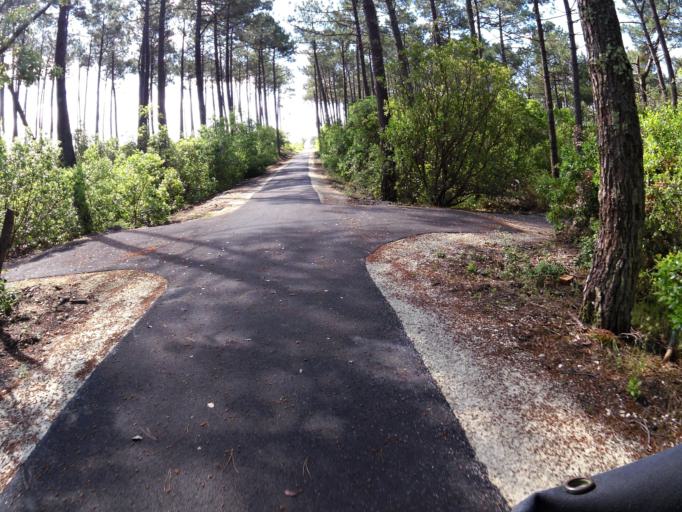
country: FR
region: Aquitaine
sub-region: Departement de la Gironde
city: Lacanau
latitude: 45.0345
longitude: -1.1812
